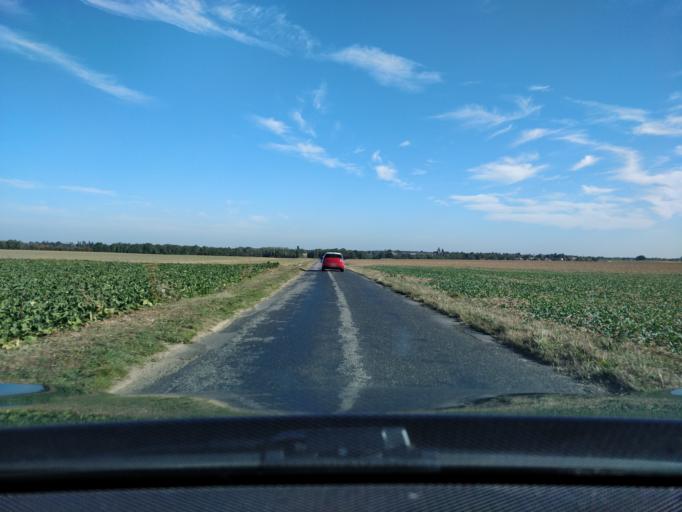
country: FR
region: Ile-de-France
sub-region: Departement de l'Essonne
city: Gometz-la-Ville
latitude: 48.6574
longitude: 2.1139
